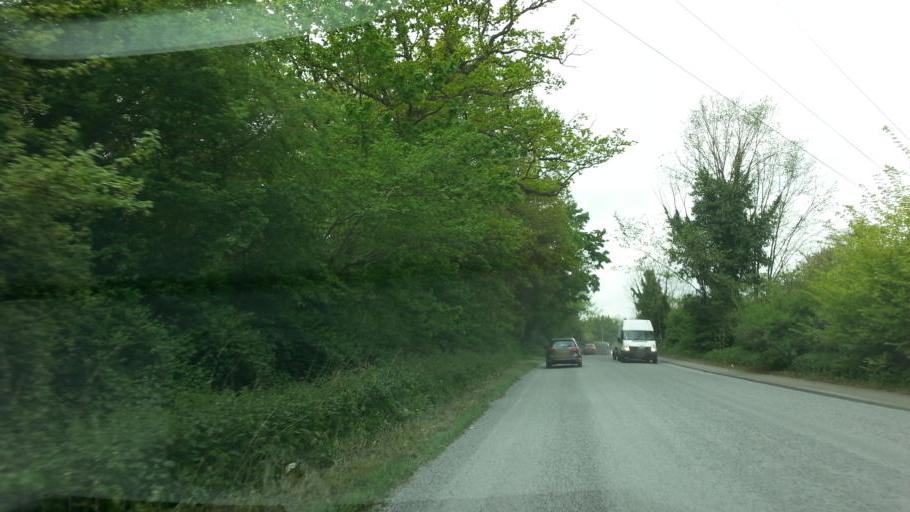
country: GB
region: England
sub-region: Suffolk
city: Bury St Edmunds
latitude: 52.2071
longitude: 0.7541
